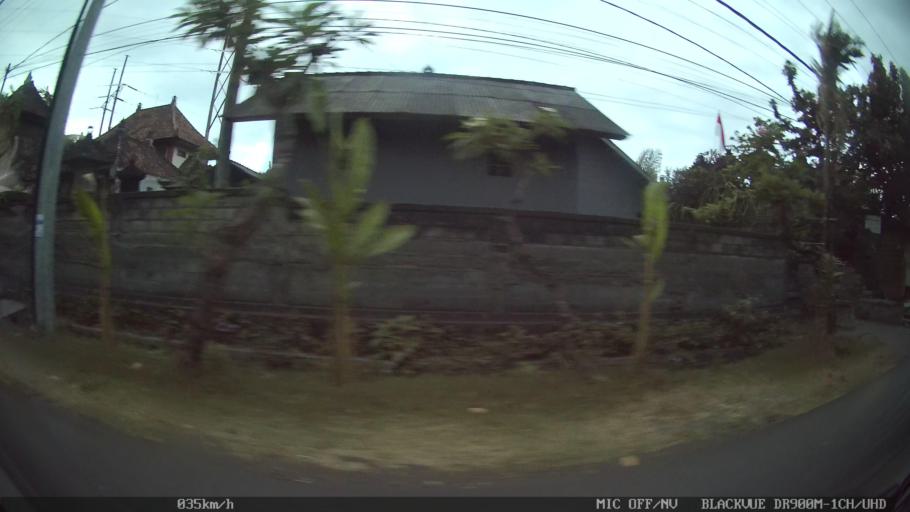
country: ID
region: Bali
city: Banjar Pasekan
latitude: -8.6287
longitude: 115.2888
